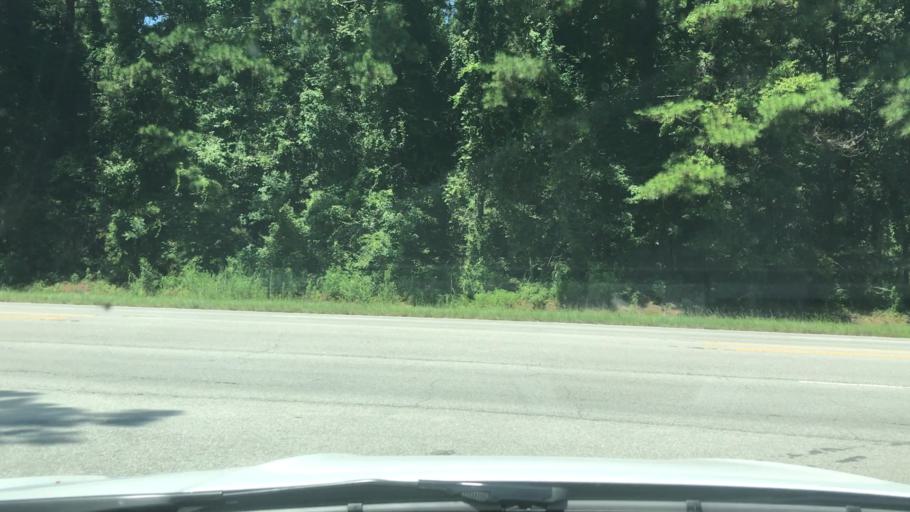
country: US
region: South Carolina
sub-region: Horry County
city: Conway
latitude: 33.8740
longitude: -79.0500
